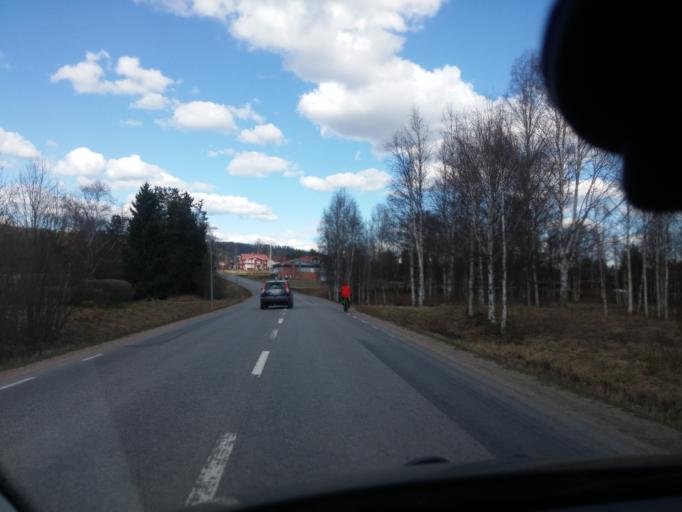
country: SE
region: Gaevleborg
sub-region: Ljusdals Kommun
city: Farila
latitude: 61.7949
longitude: 15.8353
